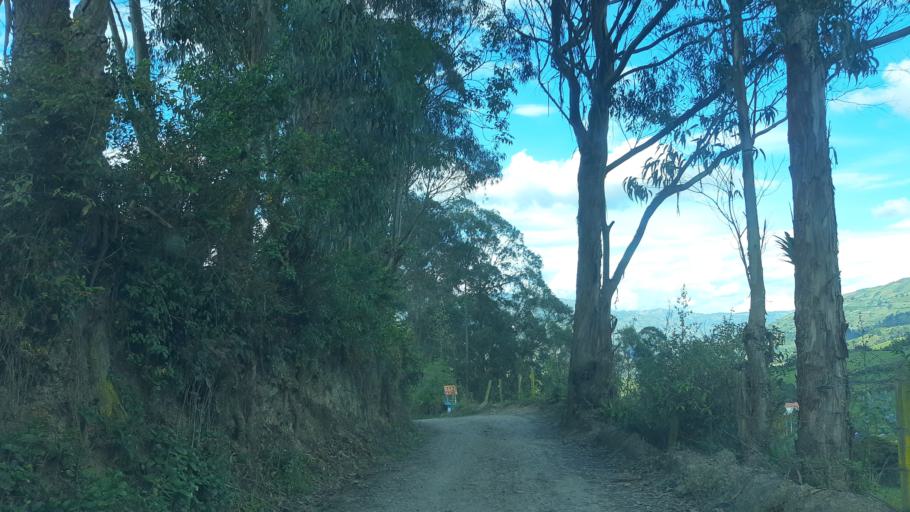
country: CO
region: Cundinamarca
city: Macheta
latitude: 5.0721
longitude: -73.6215
